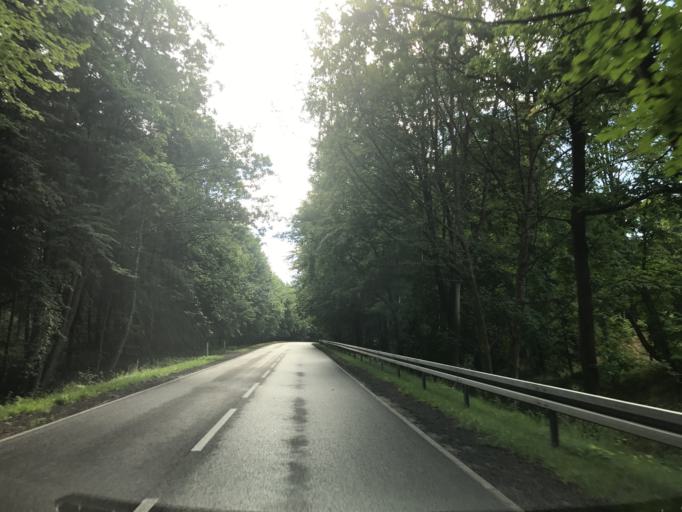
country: PL
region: West Pomeranian Voivodeship
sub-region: Powiat koszalinski
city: Sianow
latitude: 54.2098
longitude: 16.2482
